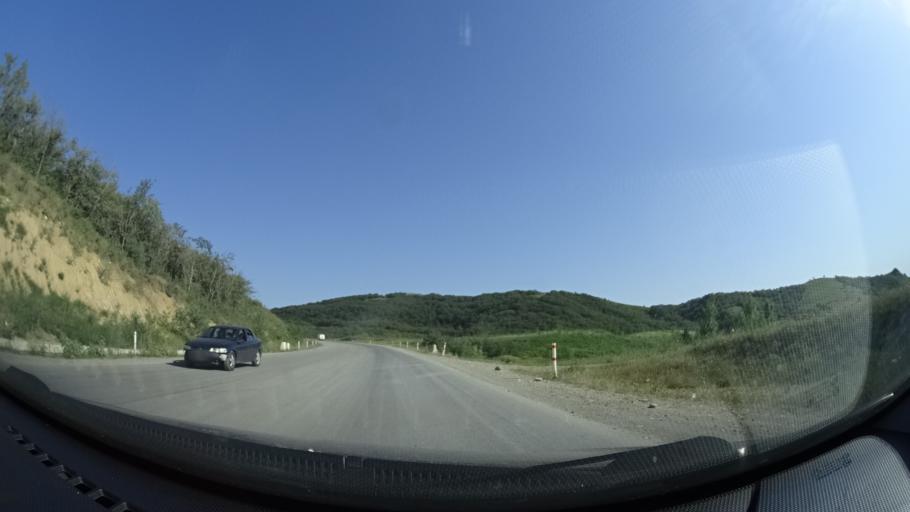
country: GE
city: Didi Lilo
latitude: 41.8010
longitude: 44.9153
